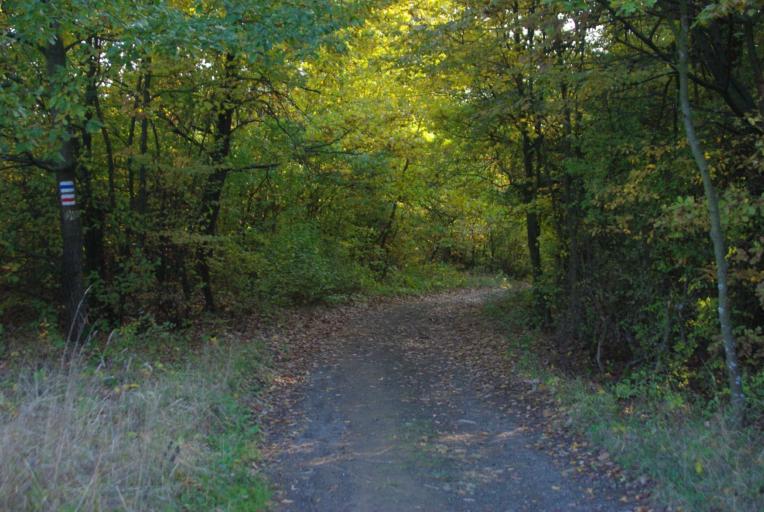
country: HU
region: Pest
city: Nagymaros
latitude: 47.8255
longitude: 18.9456
